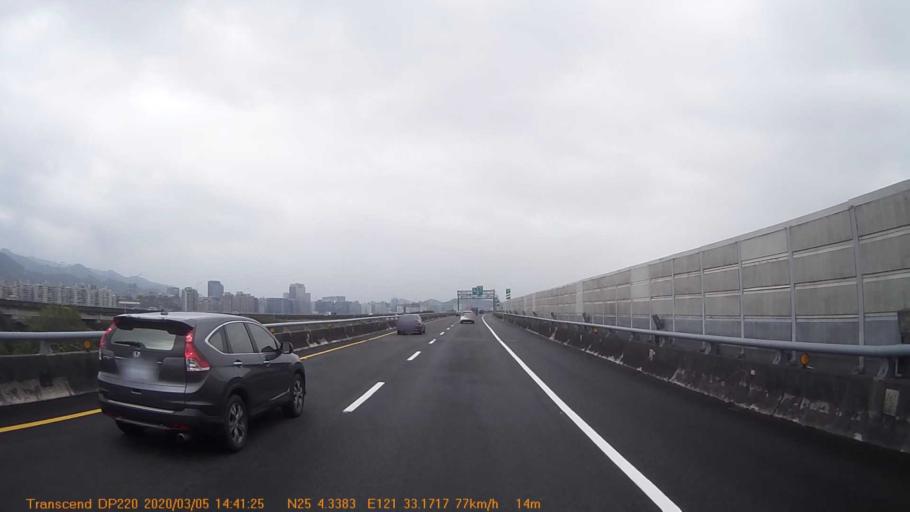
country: TW
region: Taipei
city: Taipei
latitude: 25.0721
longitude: 121.5540
